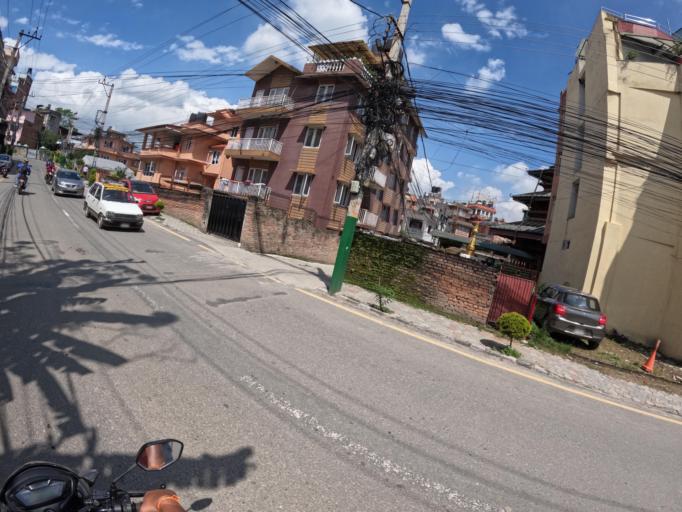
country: NP
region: Central Region
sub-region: Bagmati Zone
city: Patan
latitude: 27.6869
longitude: 85.3075
